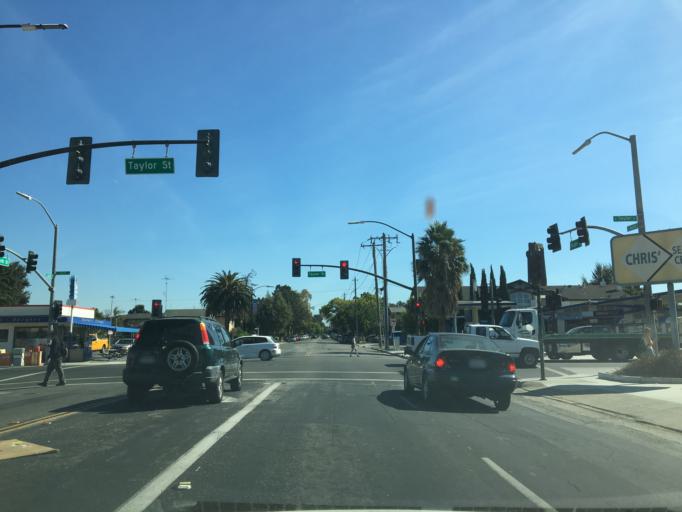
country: US
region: California
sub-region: Santa Clara County
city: San Jose
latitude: 37.3509
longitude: -121.8973
